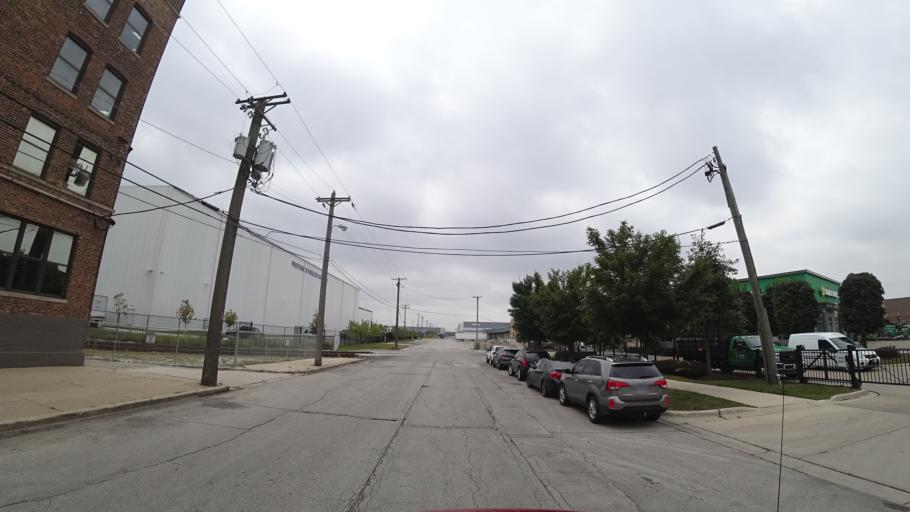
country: US
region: Illinois
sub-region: Cook County
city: Chicago
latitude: 41.8501
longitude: -87.6709
